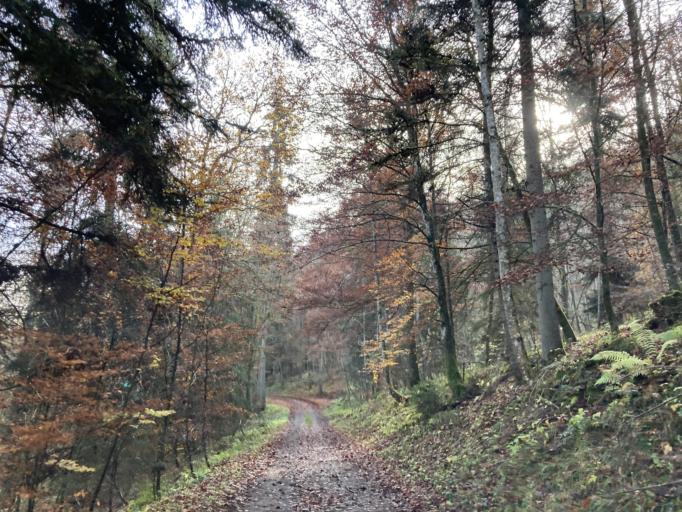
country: DE
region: Baden-Wuerttemberg
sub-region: Regierungsbezirk Stuttgart
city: Bondorf
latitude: 48.4677
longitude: 8.8495
